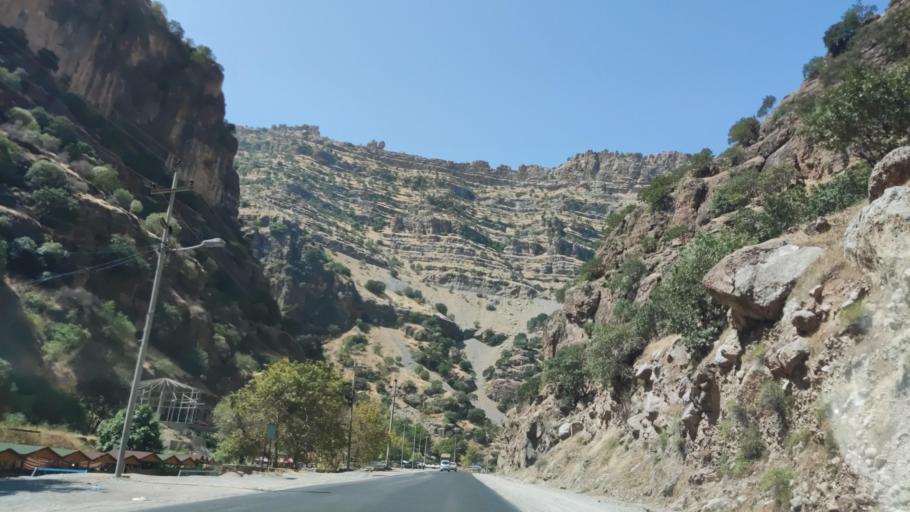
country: IQ
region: Arbil
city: Ruwandiz
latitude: 36.6288
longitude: 44.4539
